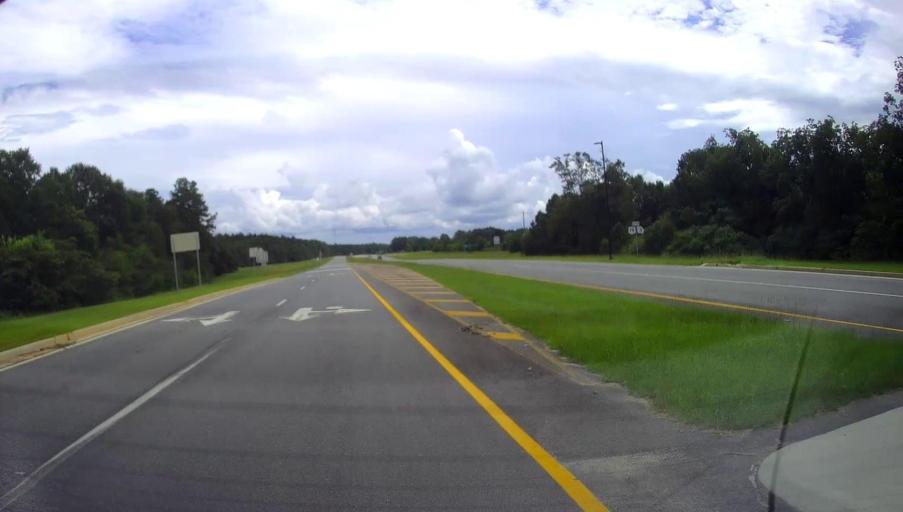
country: US
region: Georgia
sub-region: Schley County
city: Ellaville
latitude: 32.2394
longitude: -84.2961
